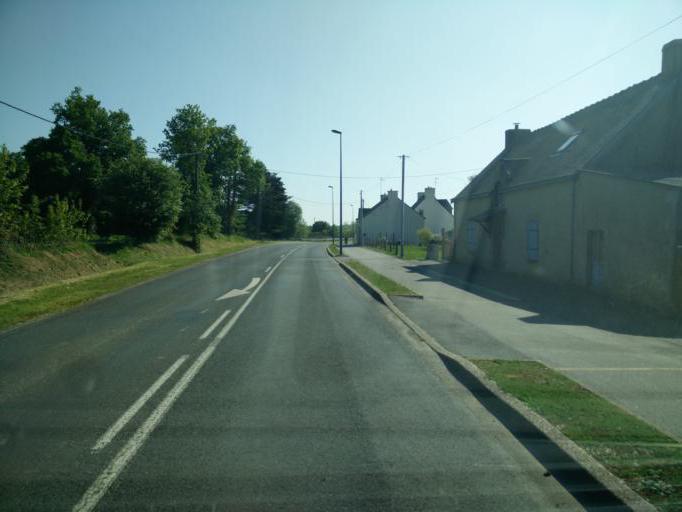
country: FR
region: Brittany
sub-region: Departement du Morbihan
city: Languidic
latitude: 47.8323
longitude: -3.1832
